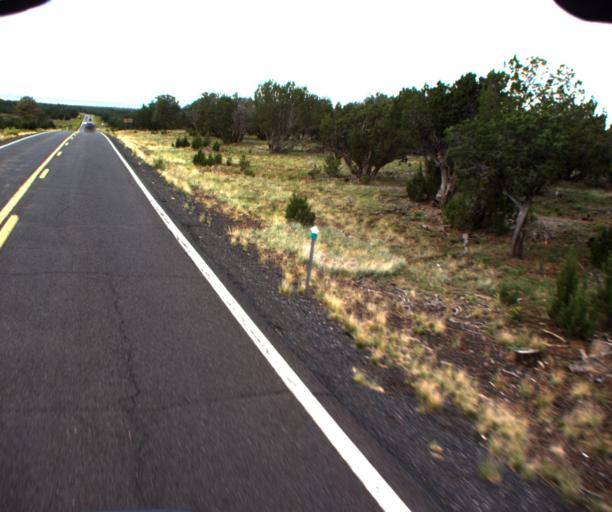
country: US
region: Arizona
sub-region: Coconino County
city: Parks
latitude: 35.5345
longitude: -111.8513
